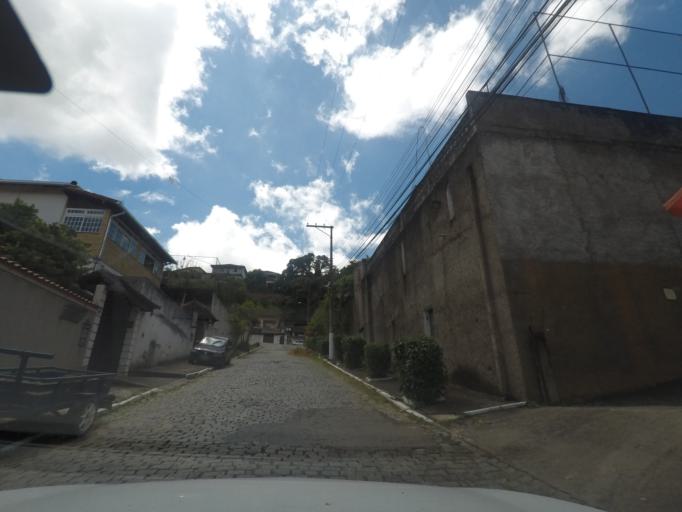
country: BR
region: Rio de Janeiro
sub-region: Teresopolis
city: Teresopolis
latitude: -22.4118
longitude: -42.9865
